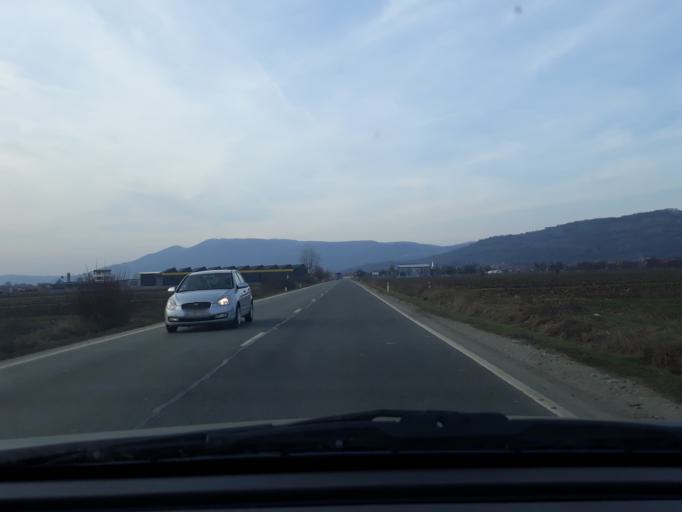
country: RO
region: Salaj
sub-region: Comuna Periceiu
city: Periceiu
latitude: 47.2214
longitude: 22.8835
